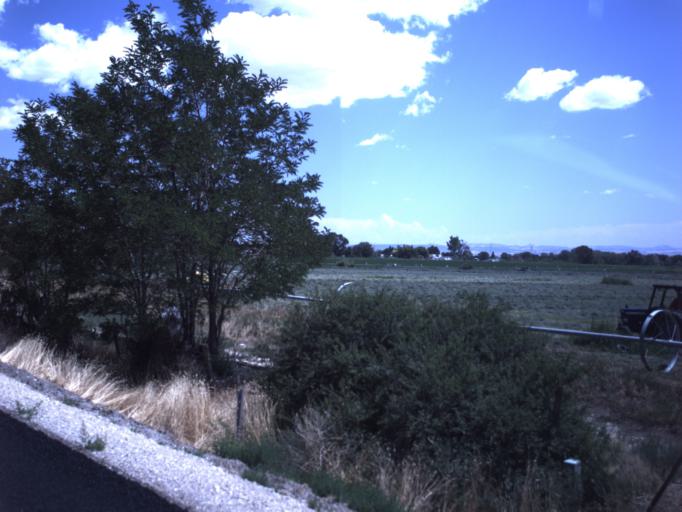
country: US
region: Utah
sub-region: Emery County
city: Orangeville
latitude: 39.2279
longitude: -111.0346
